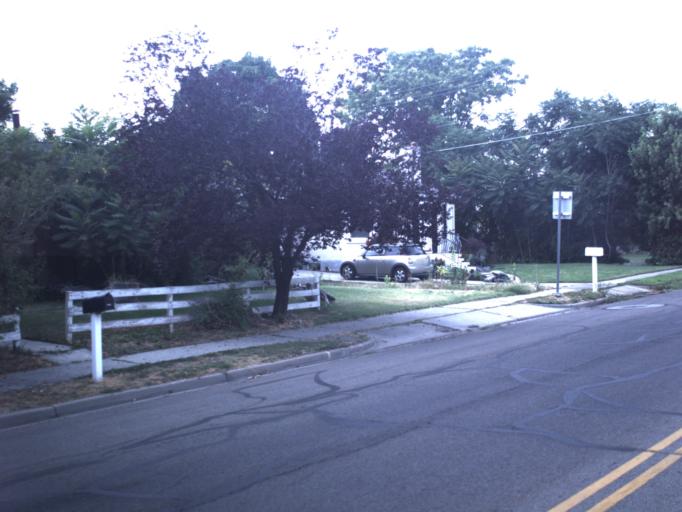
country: US
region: Utah
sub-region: Davis County
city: Bountiful
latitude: 40.8969
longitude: -111.8790
